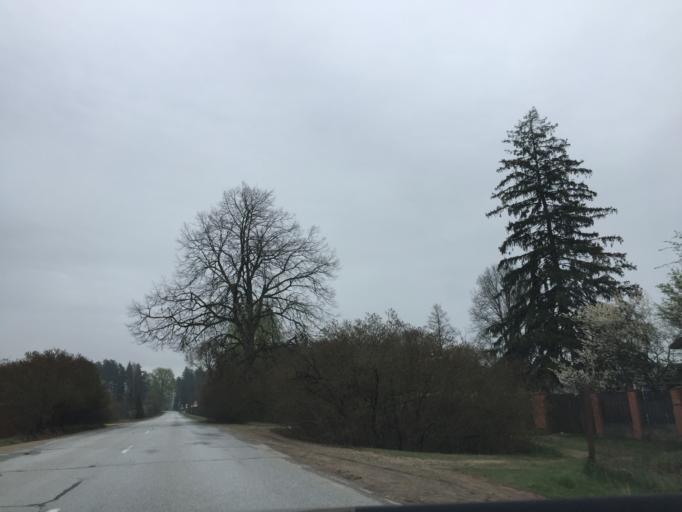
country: LV
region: Ropazu
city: Ropazi
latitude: 57.0087
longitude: 24.5575
